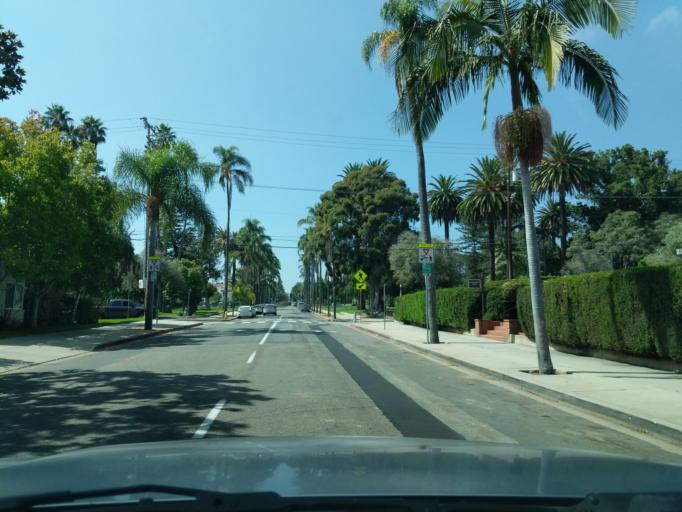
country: US
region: California
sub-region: Santa Barbara County
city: Santa Barbara
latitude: 34.4269
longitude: -119.7040
